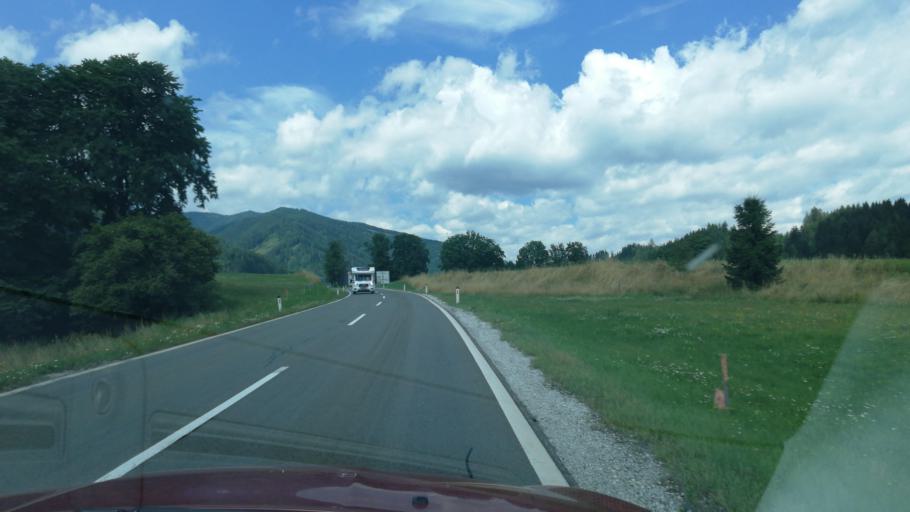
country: AT
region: Styria
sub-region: Politischer Bezirk Murtal
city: Oberzeiring
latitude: 47.2581
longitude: 14.5066
